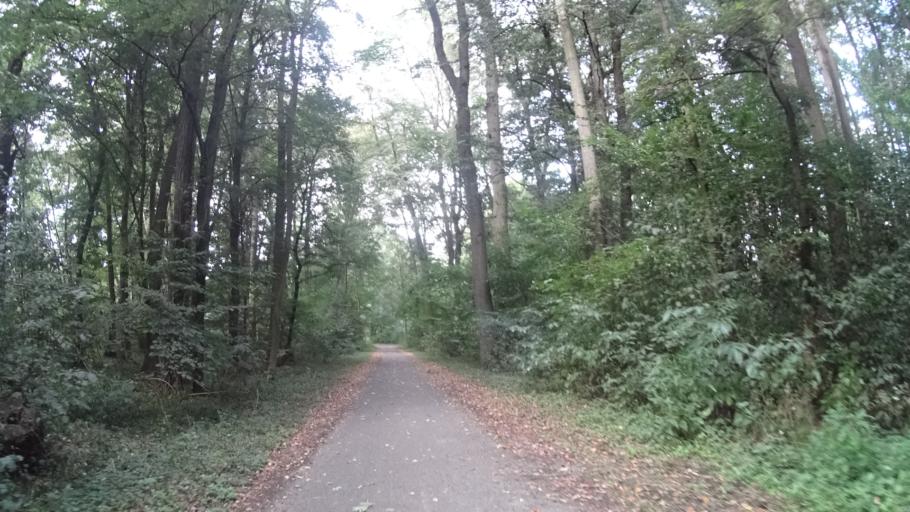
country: CZ
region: Olomoucky
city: Skrben
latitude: 49.6568
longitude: 17.1917
